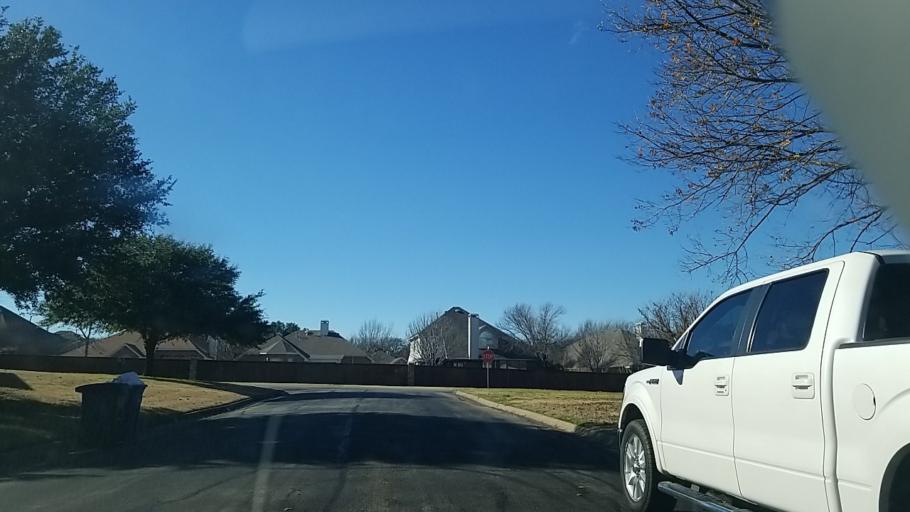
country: US
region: Texas
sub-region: Denton County
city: Corinth
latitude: 33.1580
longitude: -97.0712
